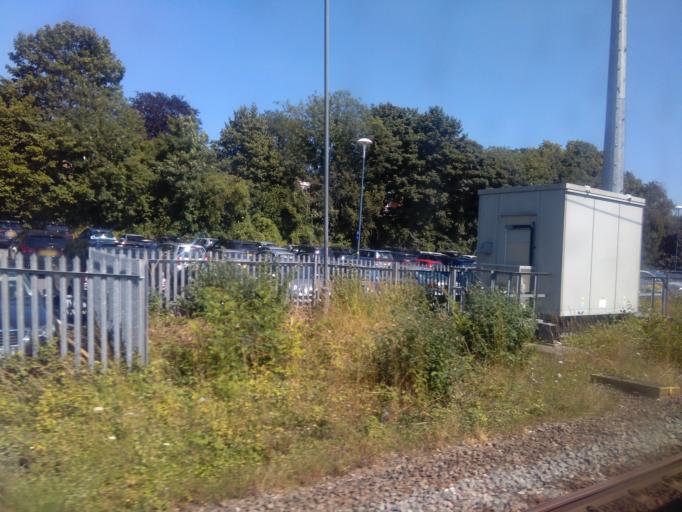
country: GB
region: England
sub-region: Hertfordshire
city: Harpenden
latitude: 51.8136
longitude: -0.3505
